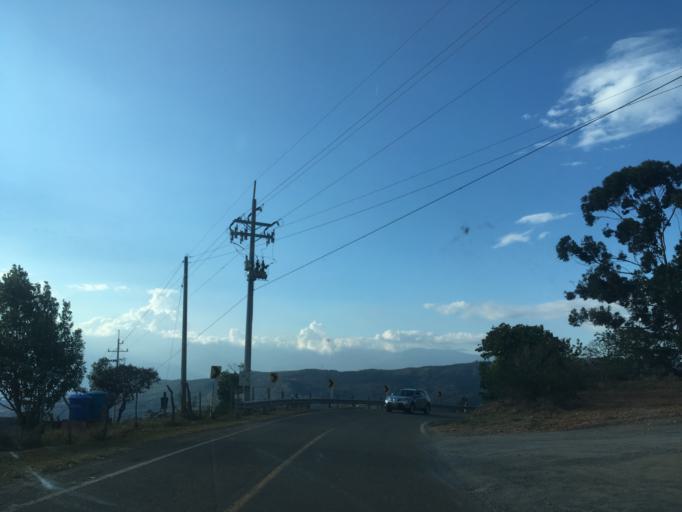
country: CO
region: Santander
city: Villanueva
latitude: 6.6313
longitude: -73.1791
